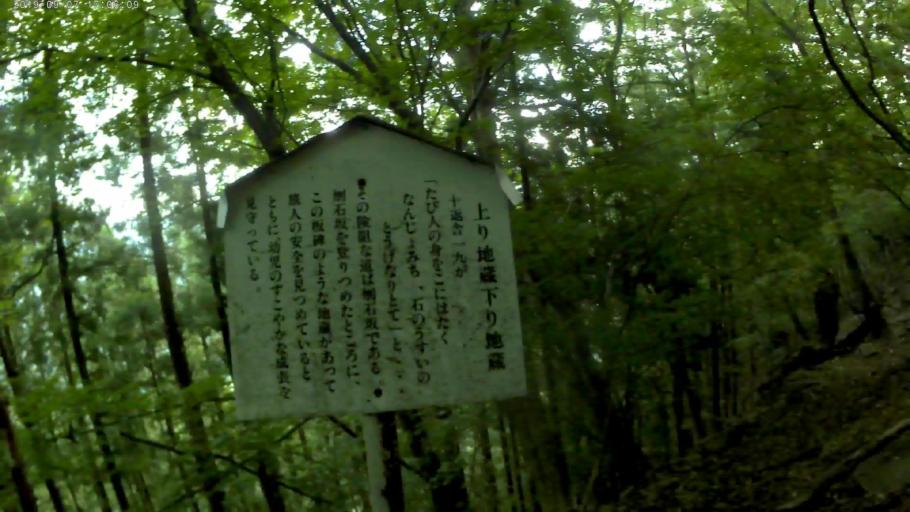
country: JP
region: Gunma
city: Annaka
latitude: 36.3586
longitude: 138.7090
